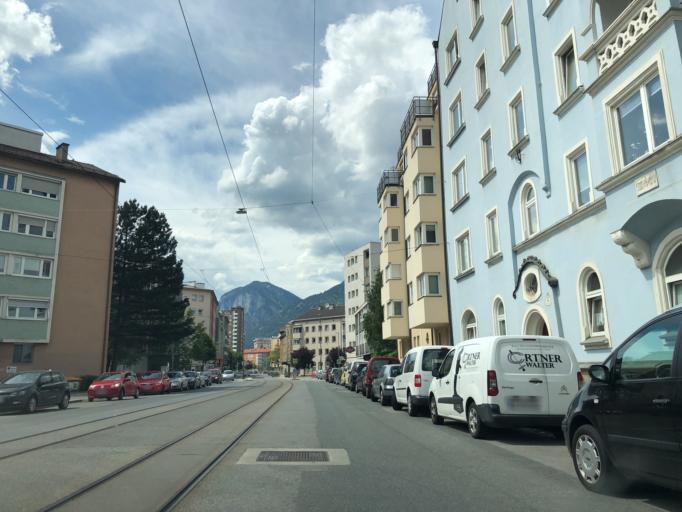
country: AT
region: Tyrol
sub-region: Innsbruck Stadt
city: Innsbruck
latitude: 47.2622
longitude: 11.4148
